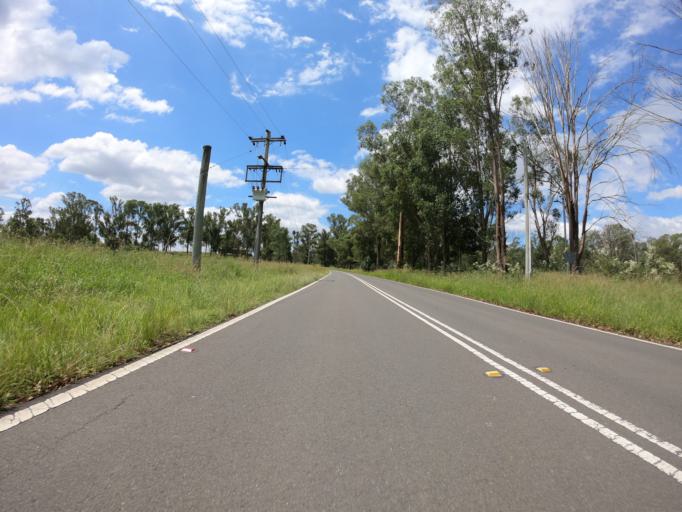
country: AU
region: New South Wales
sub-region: Penrith Municipality
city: Mulgoa
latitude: -33.8291
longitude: 150.6636
